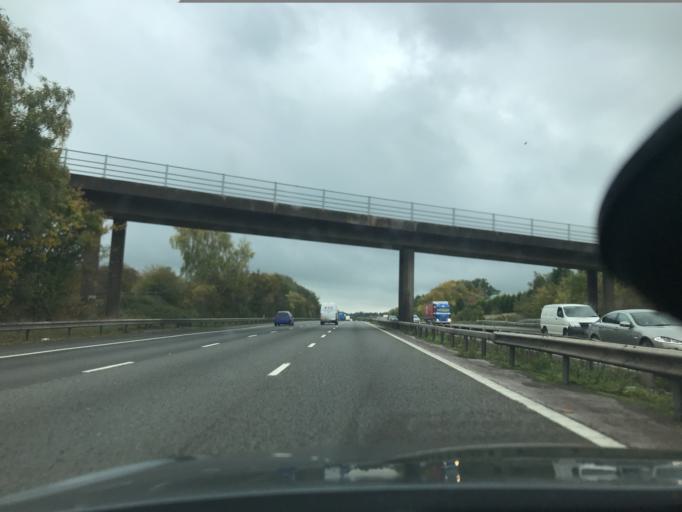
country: GB
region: England
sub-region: Warwickshire
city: Wroxall
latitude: 52.3185
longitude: -1.7186
